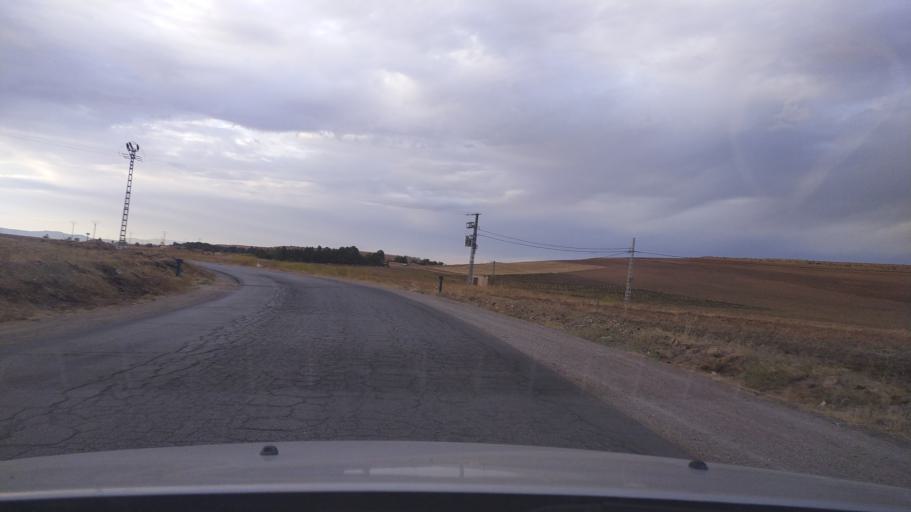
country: DZ
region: Tiaret
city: Frenda
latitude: 35.0270
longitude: 1.0980
